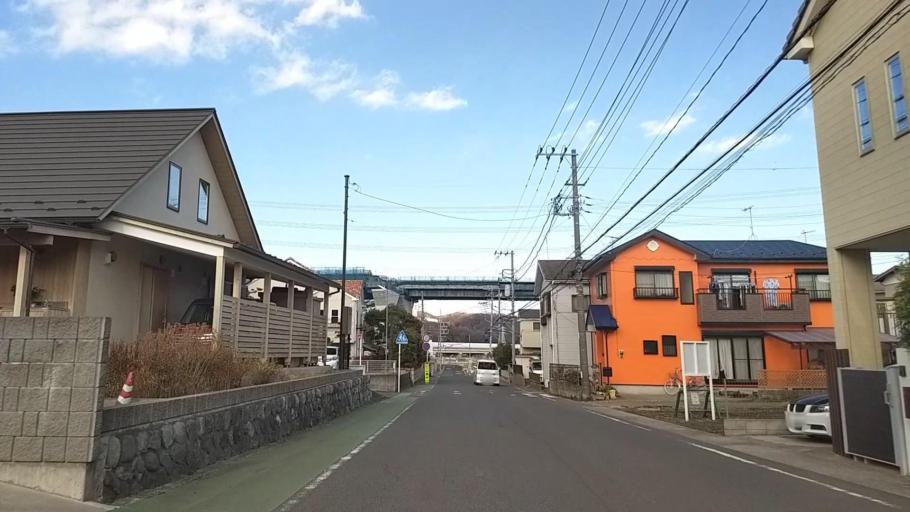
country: JP
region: Kanagawa
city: Isehara
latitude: 35.4077
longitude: 139.3179
